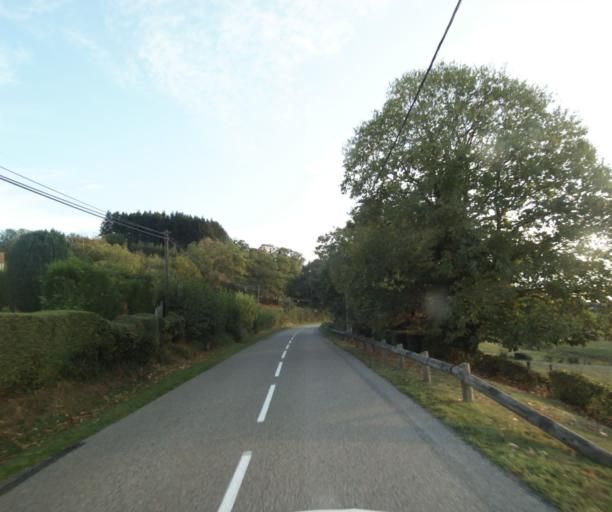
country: FR
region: Bourgogne
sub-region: Departement de Saone-et-Loire
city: Charolles
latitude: 46.4078
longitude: 4.4014
